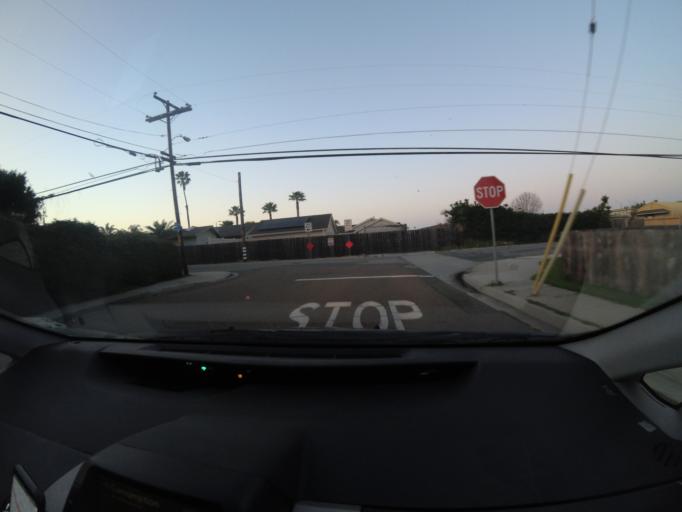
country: US
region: California
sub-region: San Diego County
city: Imperial Beach
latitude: 32.5799
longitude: -117.1165
